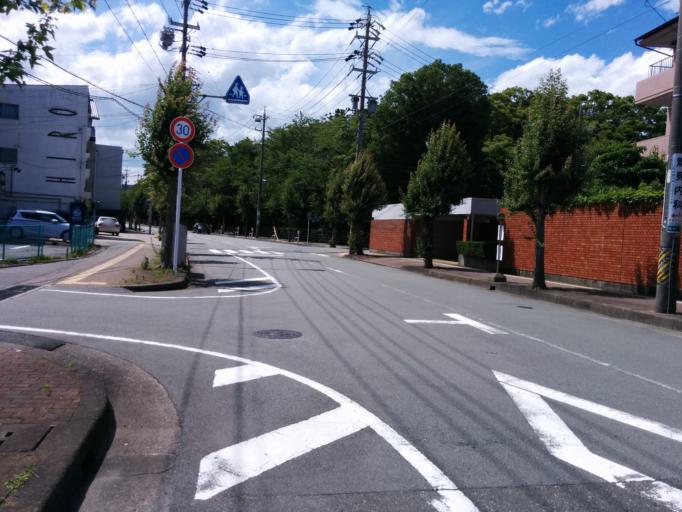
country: JP
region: Mie
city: Ise
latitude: 34.4918
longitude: 136.7066
